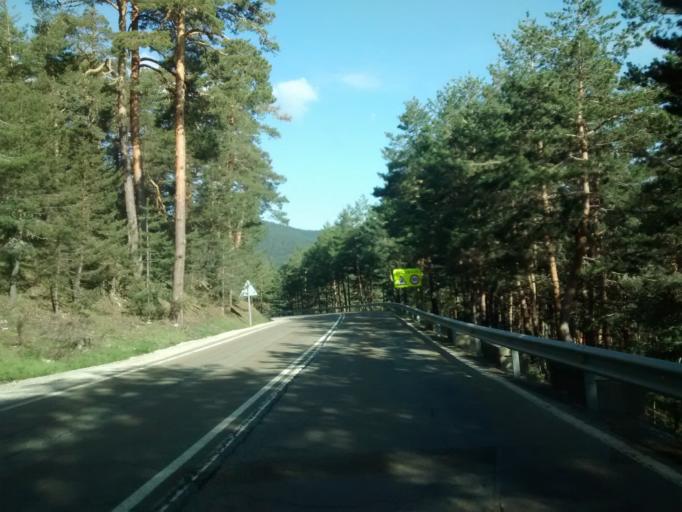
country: ES
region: Madrid
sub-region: Provincia de Madrid
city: Cercedilla
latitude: 40.8129
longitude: -4.0153
